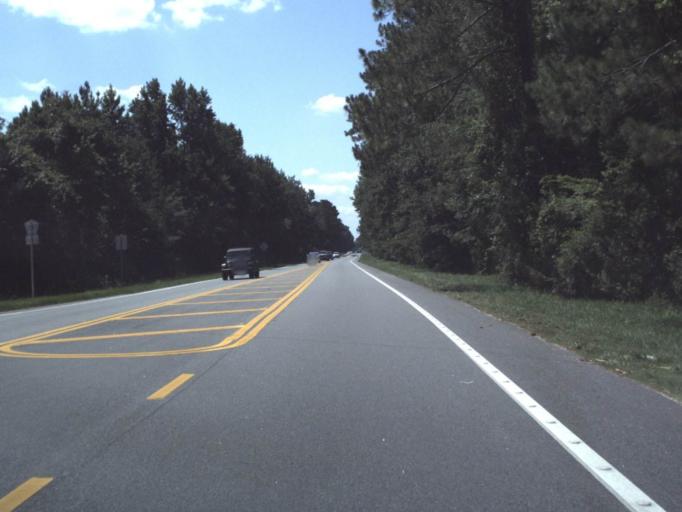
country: US
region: Florida
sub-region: Nassau County
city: Yulee
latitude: 30.6844
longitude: -81.6511
